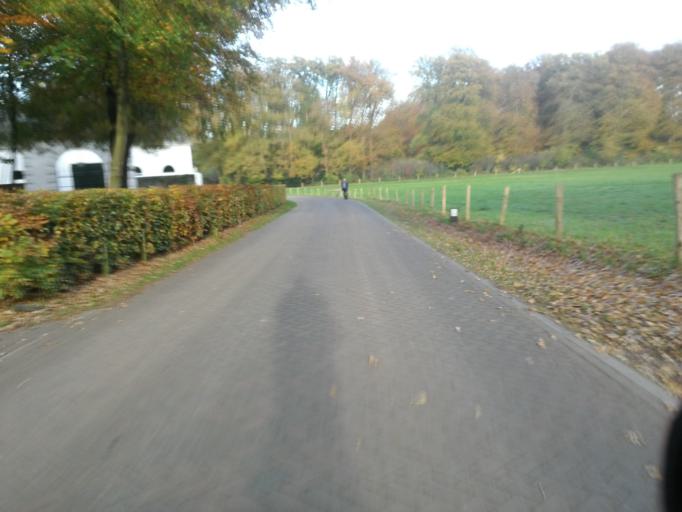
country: NL
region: Utrecht
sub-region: Gemeente Woudenberg
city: Woudenberg
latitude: 52.1053
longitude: 5.3905
